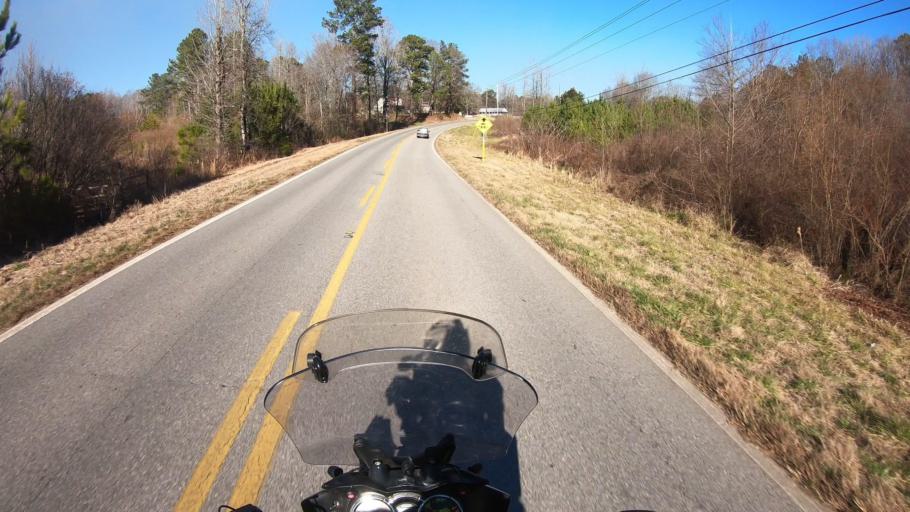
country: US
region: Alabama
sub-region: Cleburne County
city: Heflin
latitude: 33.7253
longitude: -85.4841
